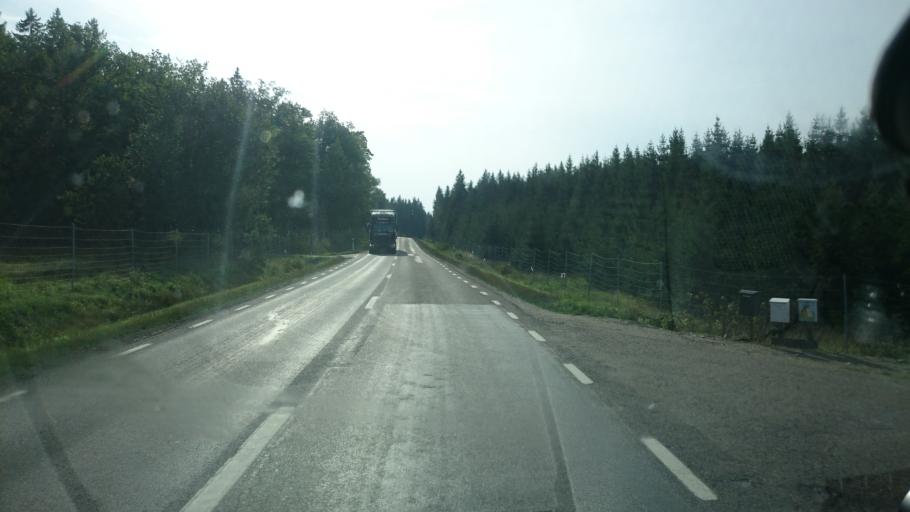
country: SE
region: Vaestra Goetaland
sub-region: Alingsas Kommun
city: Sollebrunn
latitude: 58.1476
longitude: 12.4175
